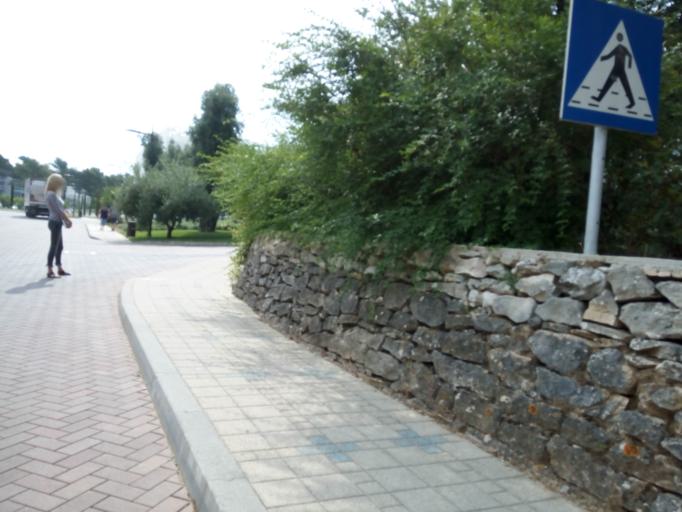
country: HR
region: Sibensko-Kniniska
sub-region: Grad Sibenik
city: Sibenik
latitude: 43.6968
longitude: 15.8871
